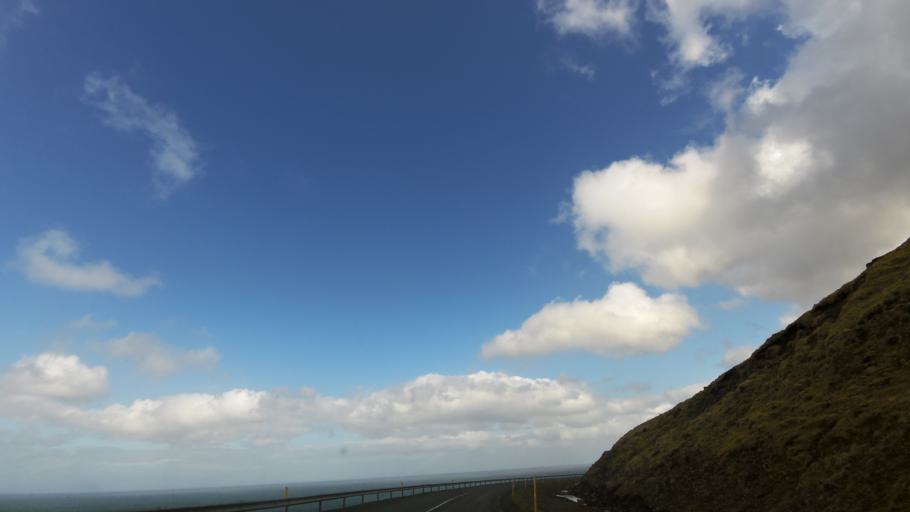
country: IS
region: West
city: Olafsvik
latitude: 64.9475
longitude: -23.4880
